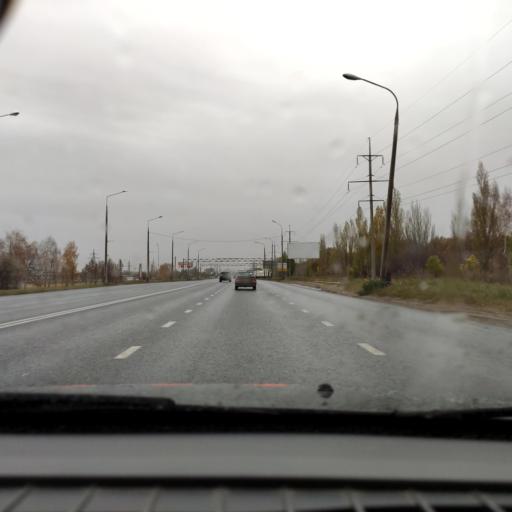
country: RU
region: Samara
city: Tol'yatti
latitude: 53.5591
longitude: 49.2889
